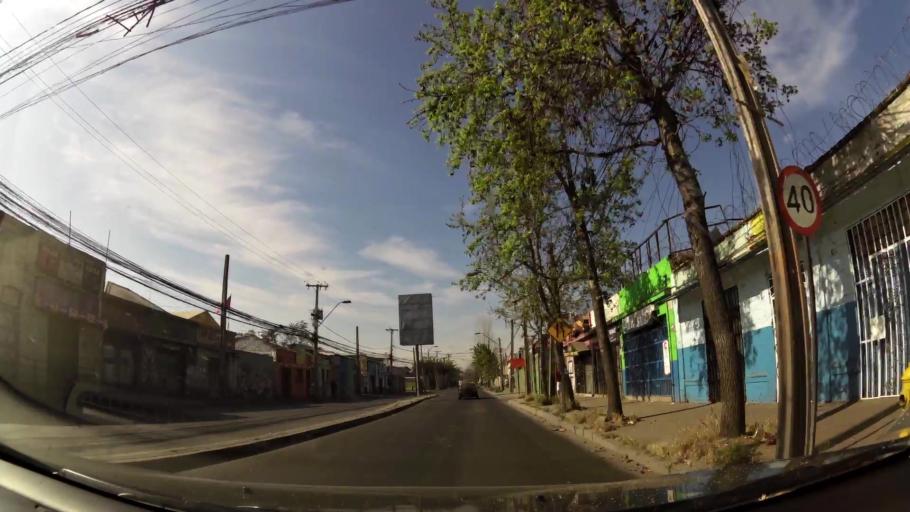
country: CL
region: Santiago Metropolitan
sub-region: Provincia de Santiago
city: Santiago
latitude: -33.3916
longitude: -70.6746
